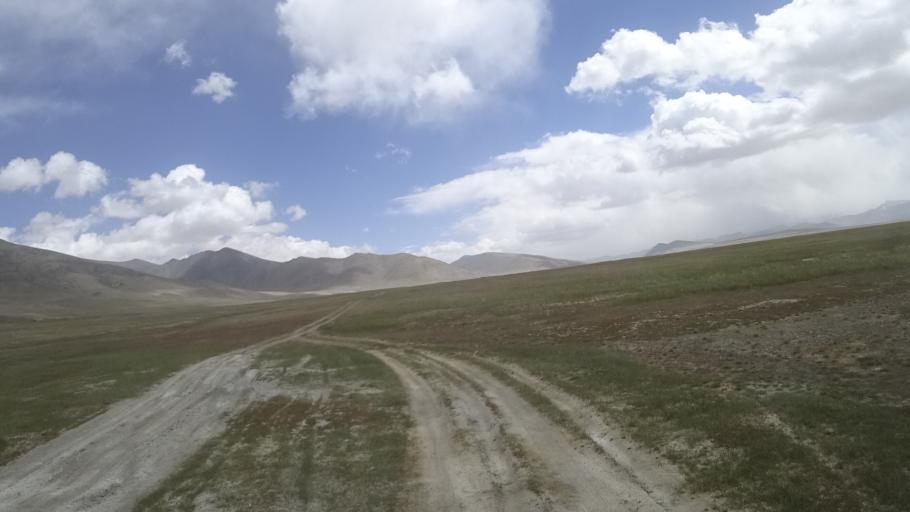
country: TJ
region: Gorno-Badakhshan
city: Murghob
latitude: 37.4839
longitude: 73.9847
